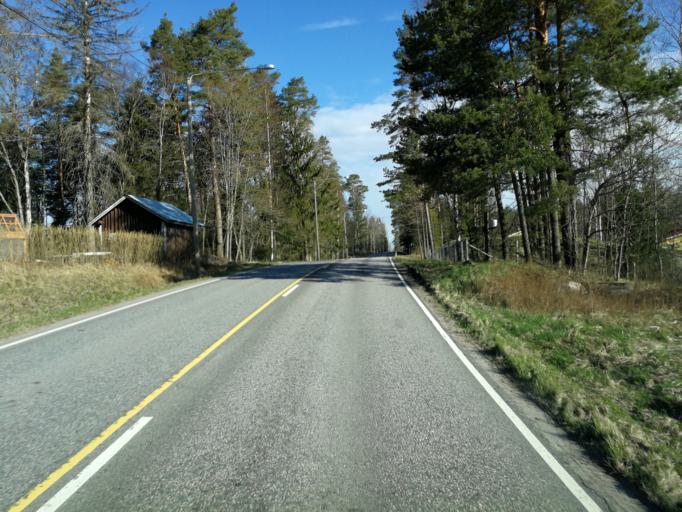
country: FI
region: Uusimaa
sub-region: Helsinki
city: Kirkkonummi
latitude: 60.2087
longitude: 24.4888
